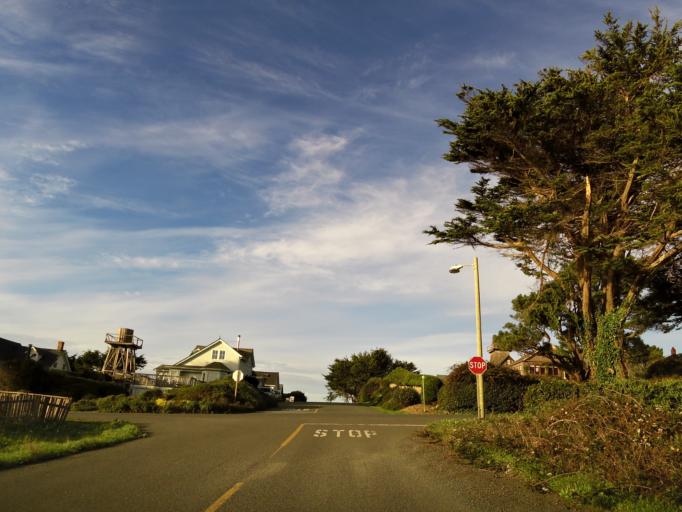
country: US
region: California
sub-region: Mendocino County
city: Fort Bragg
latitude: 39.3049
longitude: -123.8046
